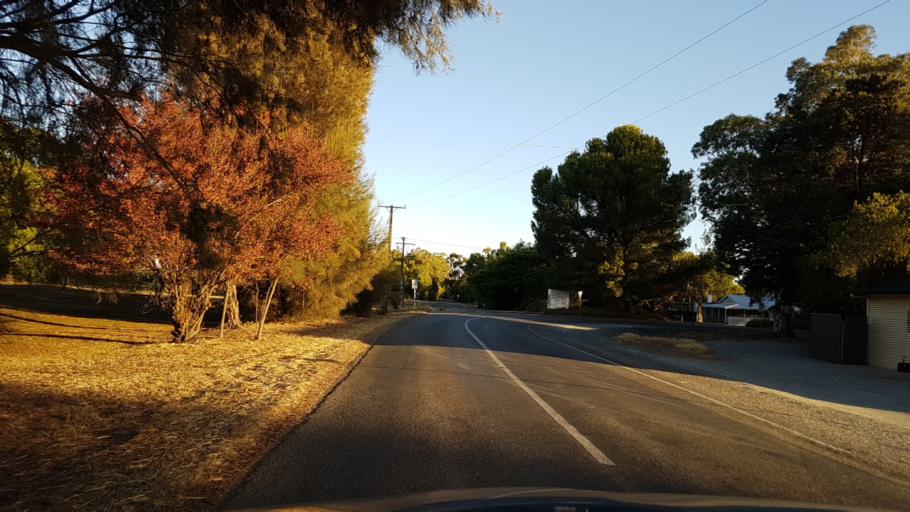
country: AU
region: South Australia
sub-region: Clare and Gilbert Valleys
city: Clare
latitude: -34.0237
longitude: 138.6883
